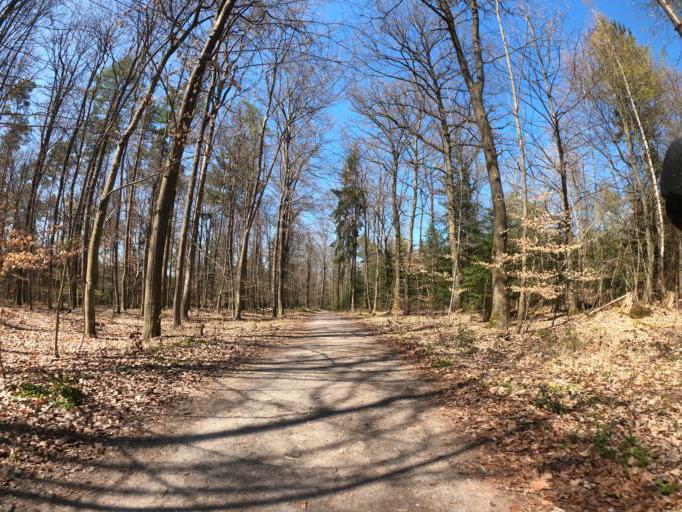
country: DE
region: Baden-Wuerttemberg
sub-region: Karlsruhe Region
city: Eutingen
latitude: 48.8901
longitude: 8.7382
